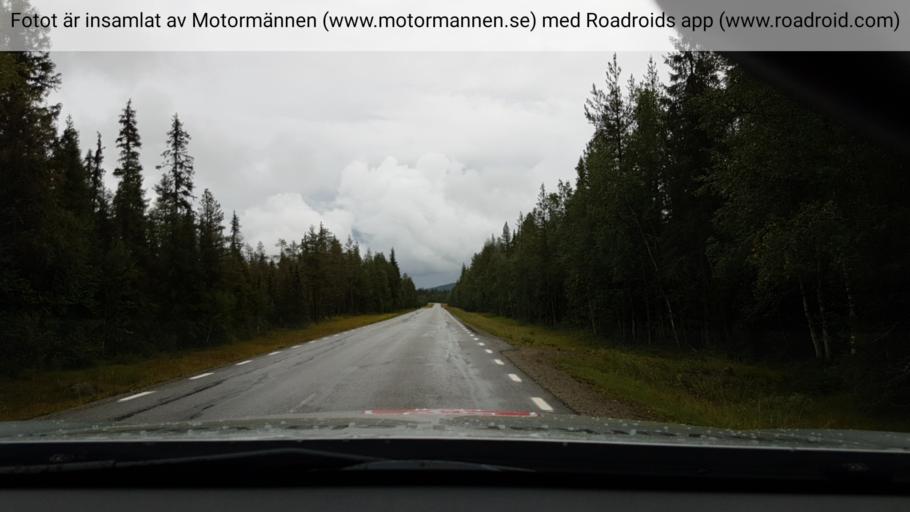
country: SE
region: Vaesterbotten
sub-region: Lycksele Kommun
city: Soderfors
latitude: 64.7018
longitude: 17.7294
